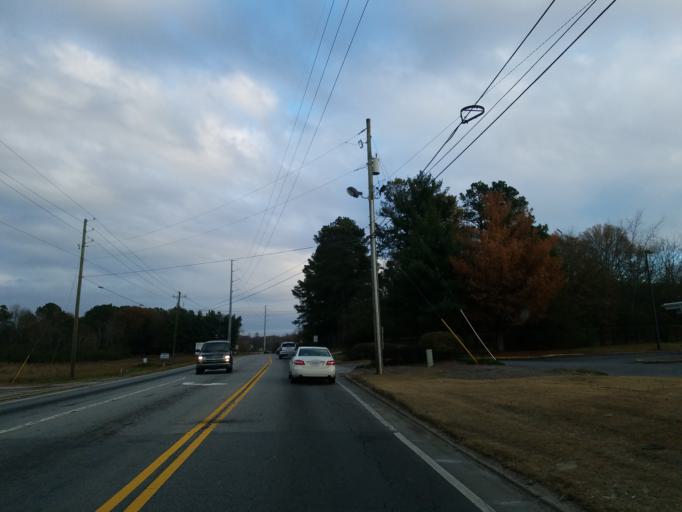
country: US
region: Georgia
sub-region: Forsyth County
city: Cumming
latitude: 34.2715
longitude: -84.1006
